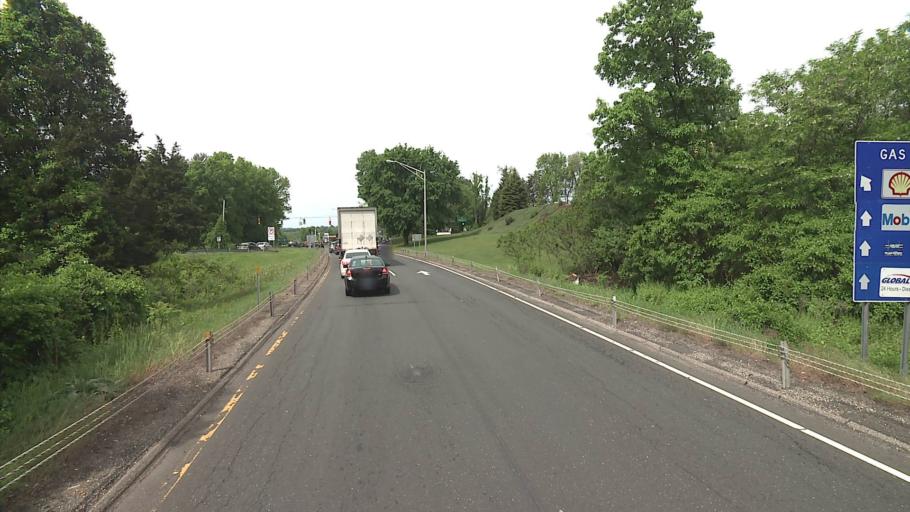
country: US
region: Connecticut
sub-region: Fairfield County
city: Bethel
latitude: 41.4164
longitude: -73.4058
